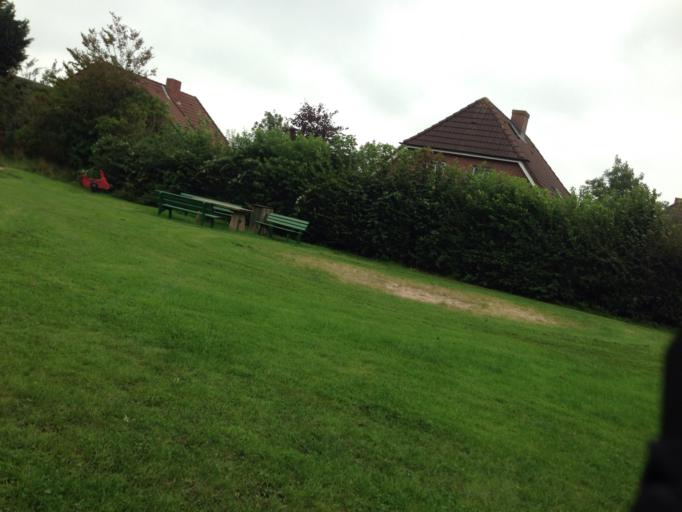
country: DE
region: Schleswig-Holstein
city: Wrixum
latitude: 54.6955
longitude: 8.5533
